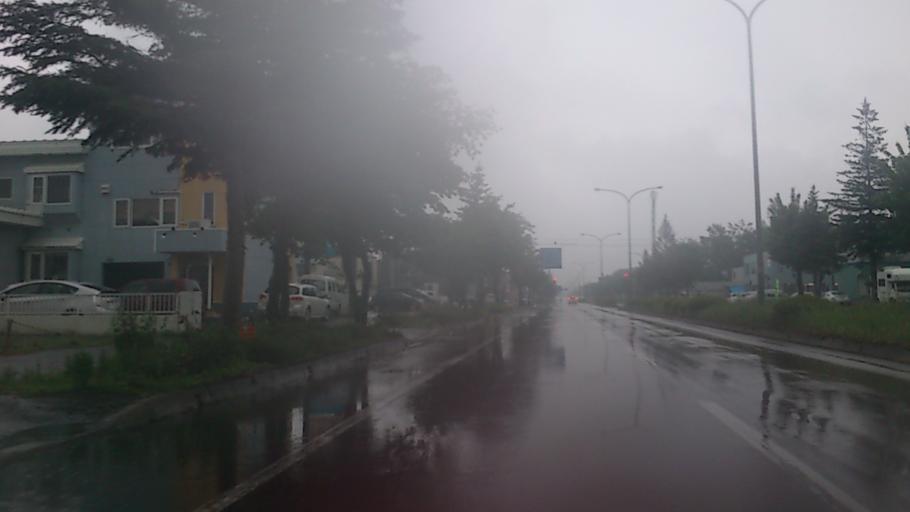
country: JP
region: Hokkaido
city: Obihiro
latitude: 42.9097
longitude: 143.1316
